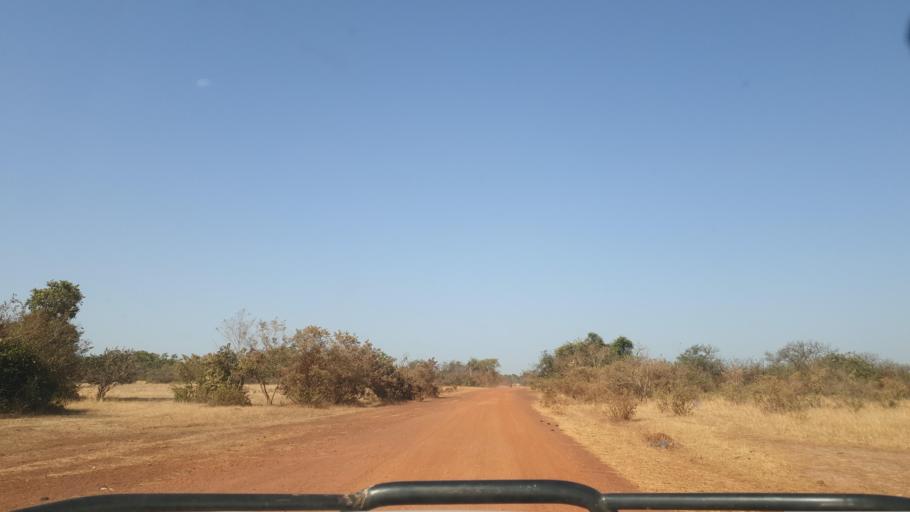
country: ML
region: Sikasso
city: Bougouni
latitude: 11.8180
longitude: -6.9417
